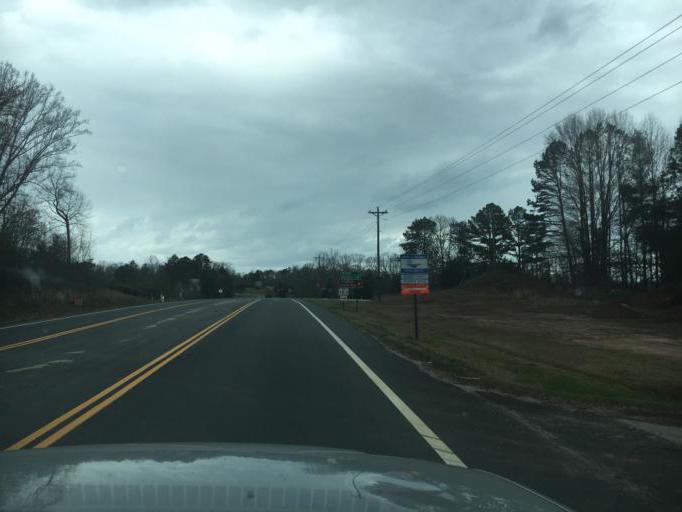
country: US
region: South Carolina
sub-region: Oconee County
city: Walhalla
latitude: 34.8028
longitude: -83.0306
